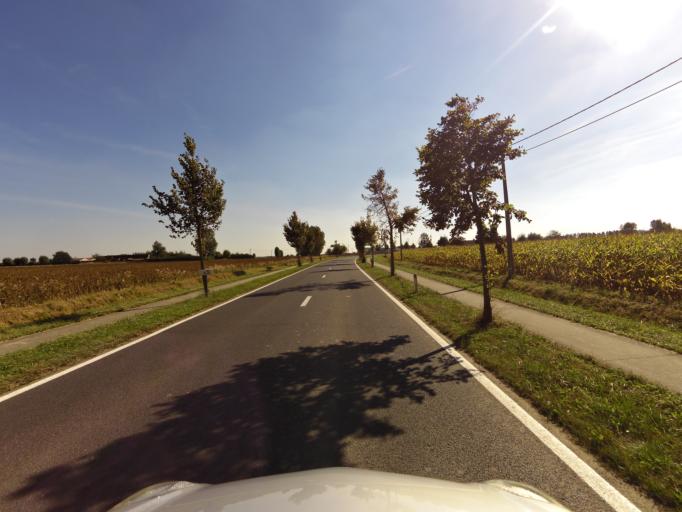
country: BE
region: Flanders
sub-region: Provincie West-Vlaanderen
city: Poperinge
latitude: 50.8947
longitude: 2.7399
